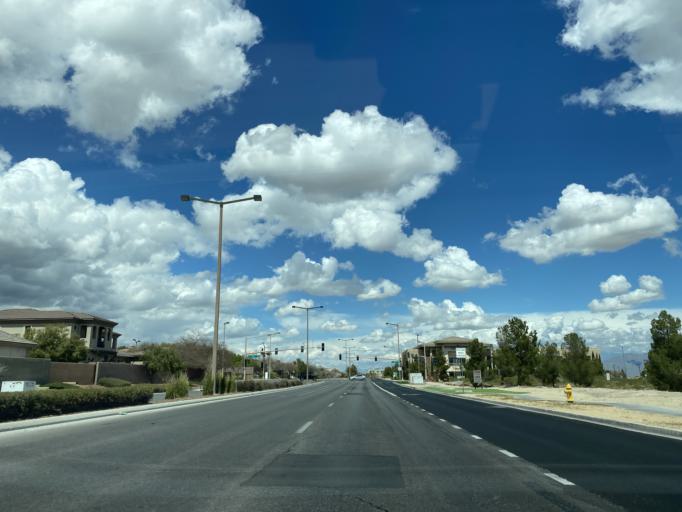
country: US
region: Nevada
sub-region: Clark County
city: Summerlin South
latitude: 36.1667
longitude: -115.3150
